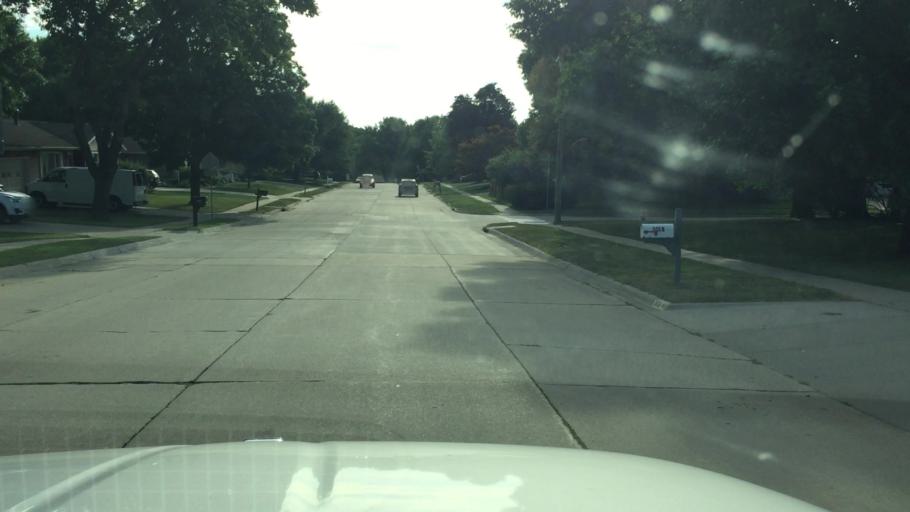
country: US
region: Iowa
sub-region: Johnson County
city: Iowa City
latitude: 41.6611
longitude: -91.4886
